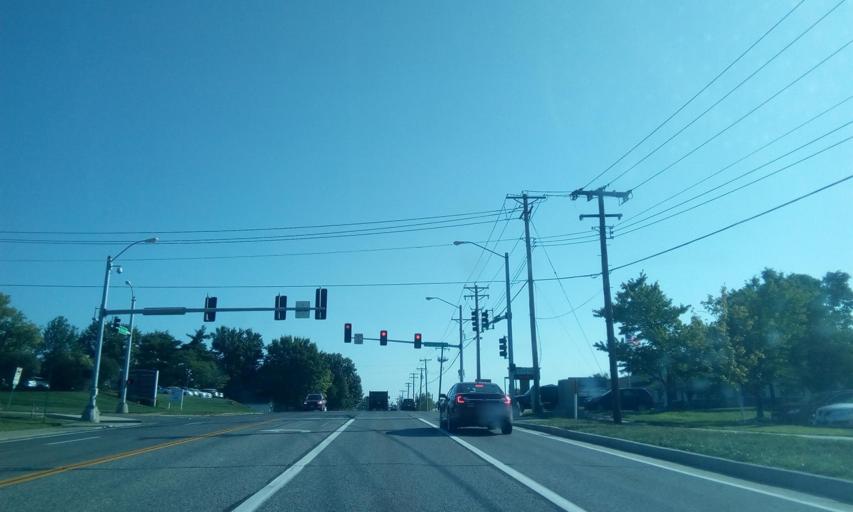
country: US
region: Missouri
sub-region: Saint Louis County
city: Concord
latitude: 38.5171
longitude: -90.3664
